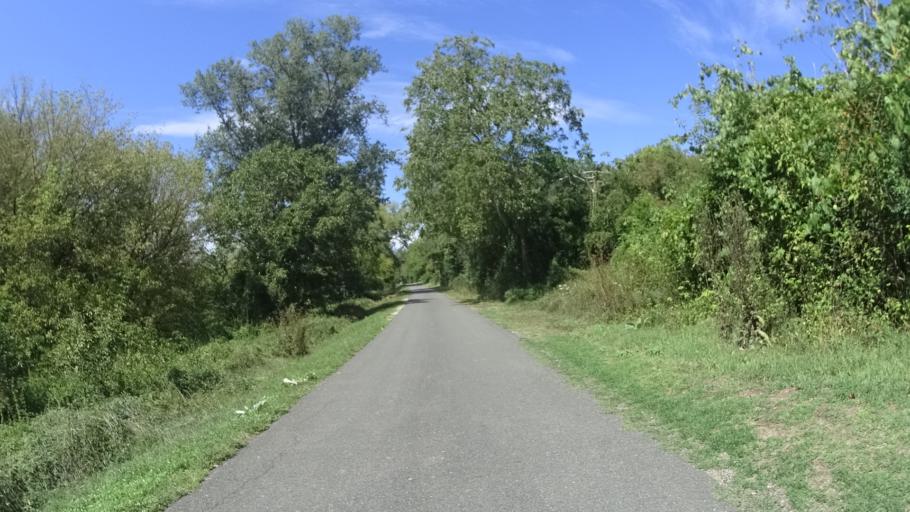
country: FR
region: Centre
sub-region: Departement du Loiret
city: Bonny-sur-Loire
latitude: 47.5826
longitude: 2.8026
